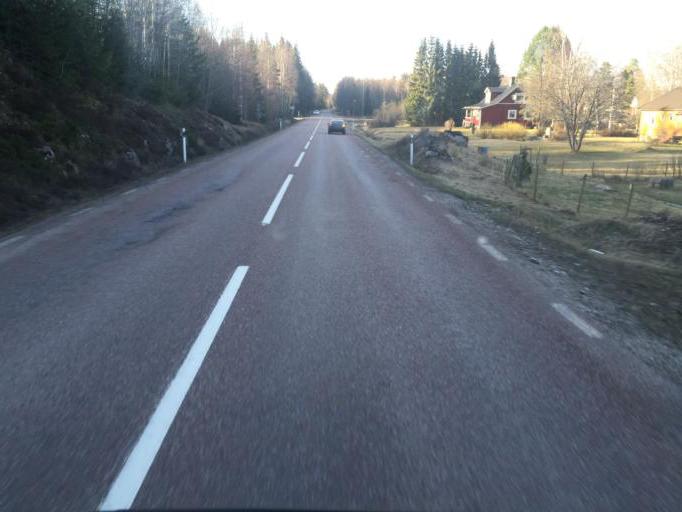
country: SE
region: Dalarna
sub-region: Gagnefs Kommun
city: Mockfjard
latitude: 60.4967
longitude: 14.7835
